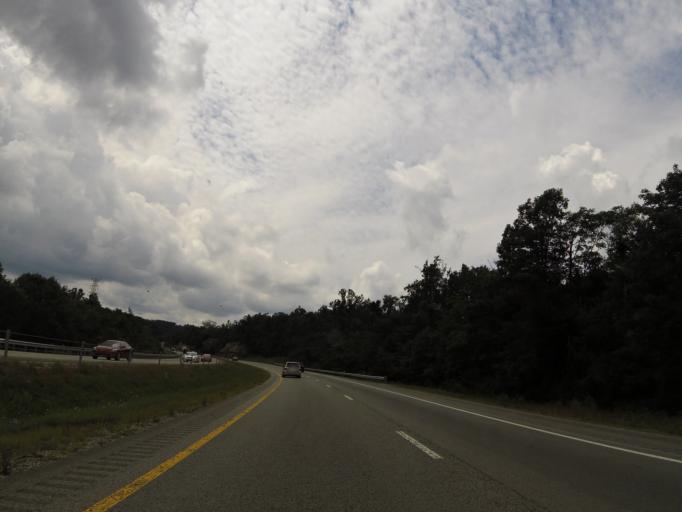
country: US
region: Tennessee
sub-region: Putnam County
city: Monterey
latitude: 36.1407
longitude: -85.3068
